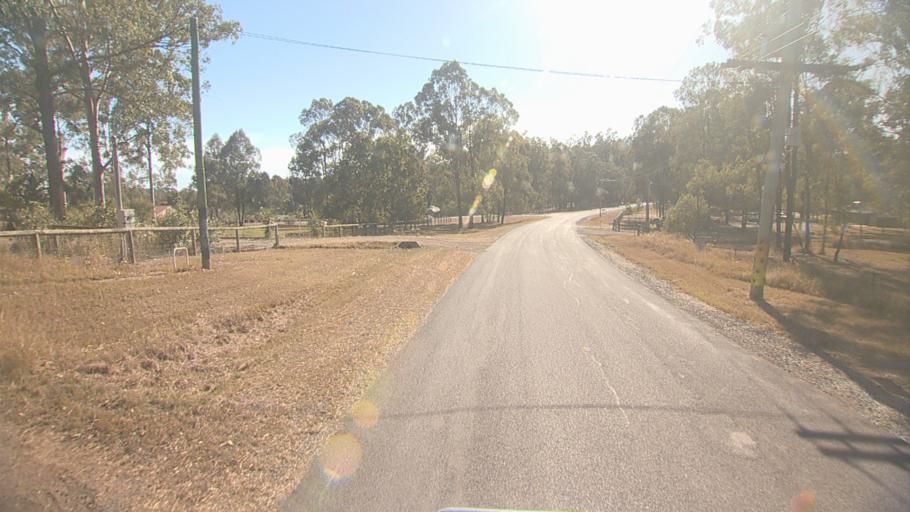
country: AU
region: Queensland
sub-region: Logan
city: Cedar Vale
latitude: -27.8578
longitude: 152.9910
